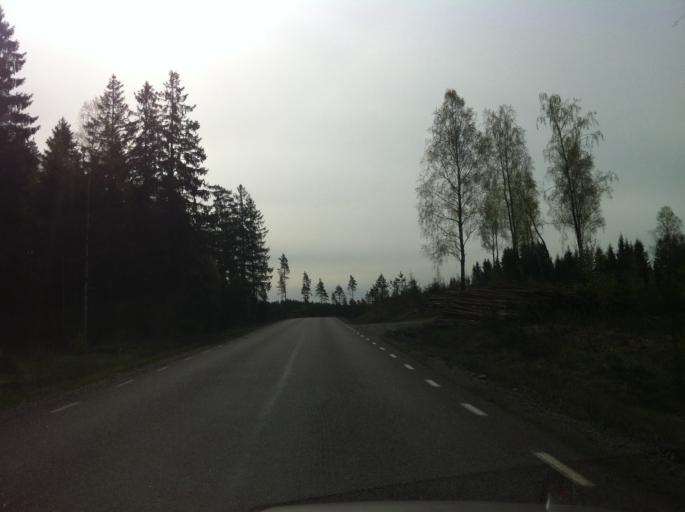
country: SE
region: Vaestra Goetaland
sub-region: Bollebygds Kommun
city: Bollebygd
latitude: 57.6544
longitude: 12.6080
